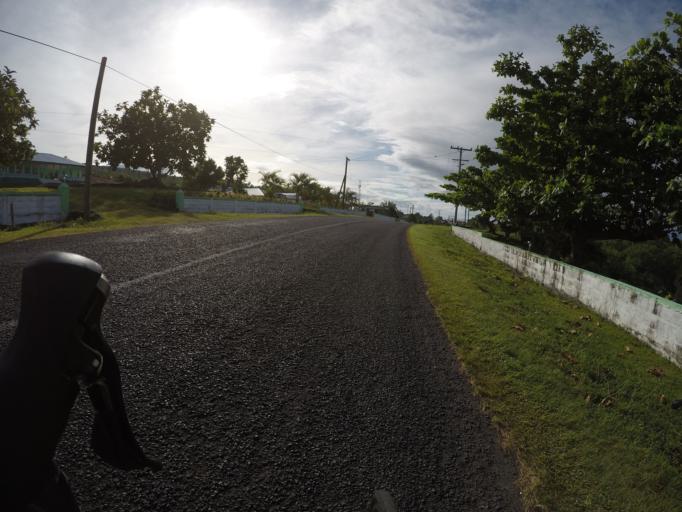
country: WS
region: Vaisigano
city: Asau
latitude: -13.6416
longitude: -172.6690
